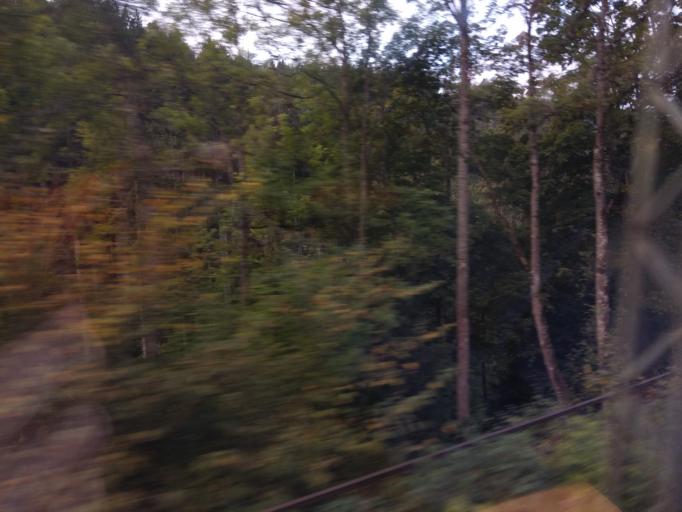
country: DE
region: Baden-Wuerttemberg
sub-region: Freiburg Region
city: Hinterzarten
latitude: 47.9122
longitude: 8.0910
